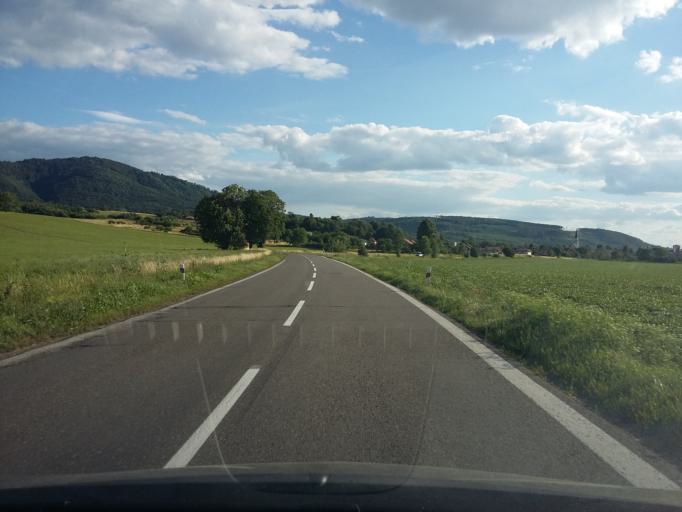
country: SK
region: Bratislavsky
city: Modra
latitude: 48.4718
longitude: 17.2414
